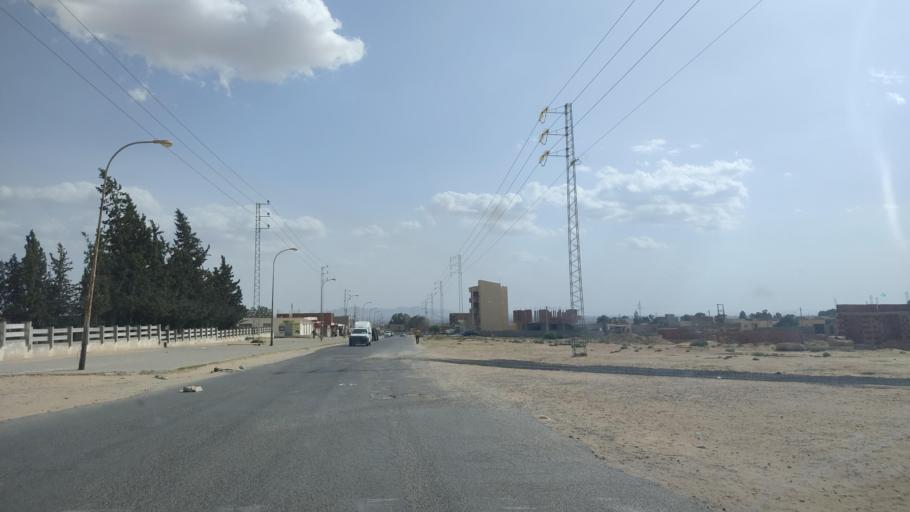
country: TN
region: Sidi Bu Zayd
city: Sidi Bouzid
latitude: 35.1048
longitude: 9.5368
